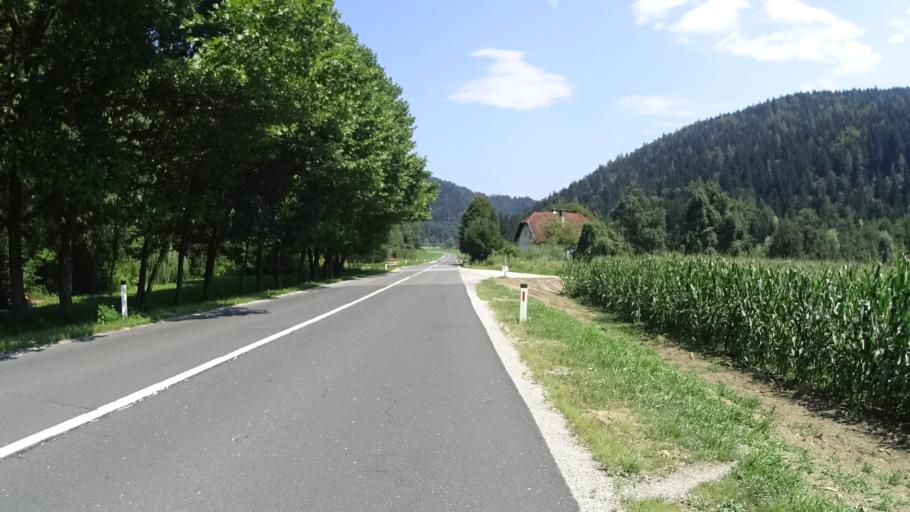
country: SI
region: Mezica
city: Mezica
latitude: 46.5467
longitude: 14.8816
